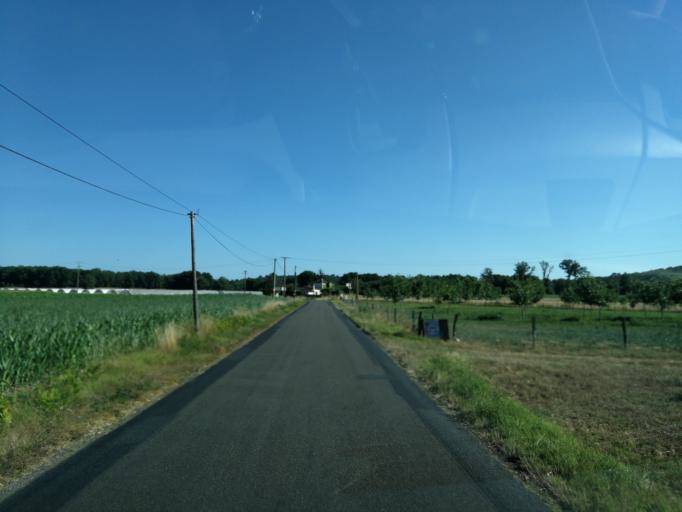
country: FR
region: Midi-Pyrenees
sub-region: Departement du Lot
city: Gourdon
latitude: 44.7925
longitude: 1.3683
